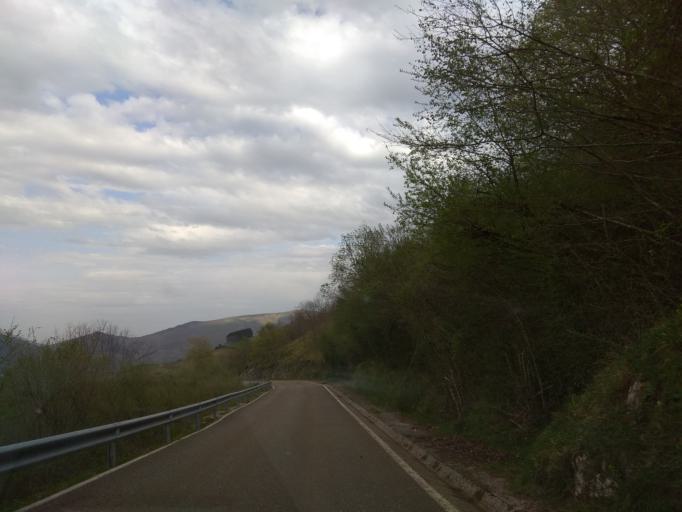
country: ES
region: Cantabria
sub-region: Provincia de Cantabria
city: Cabezon de Liebana
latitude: 43.2496
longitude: -4.5294
